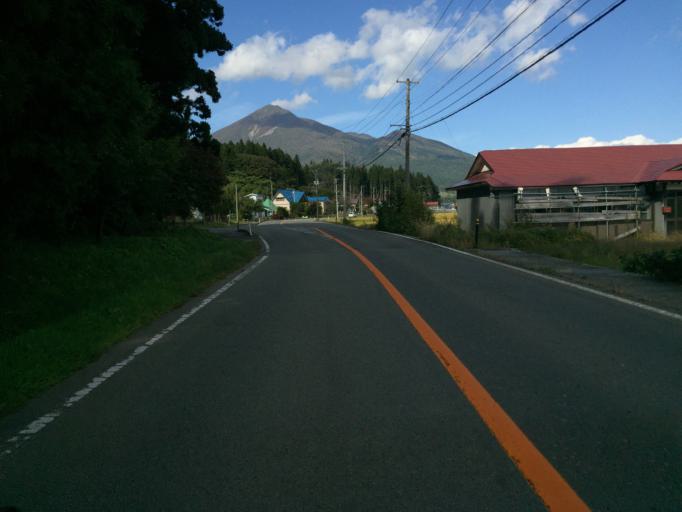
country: JP
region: Fukushima
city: Inawashiro
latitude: 37.5391
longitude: 140.0629
